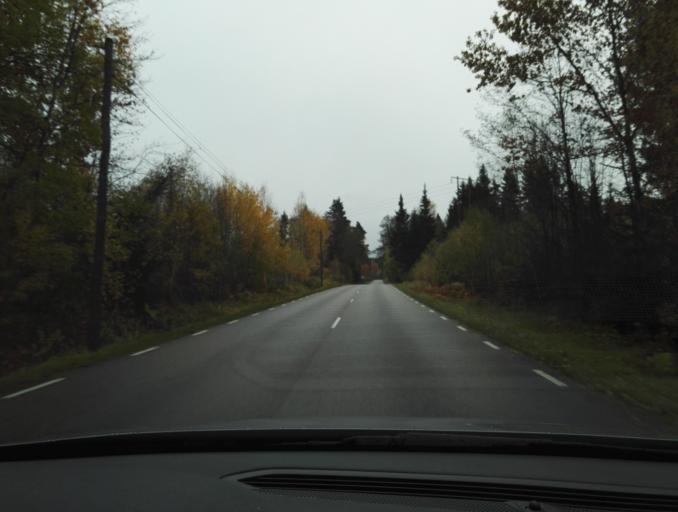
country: SE
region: Kronoberg
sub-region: Vaxjo Kommun
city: Rottne
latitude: 57.0309
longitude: 14.8126
